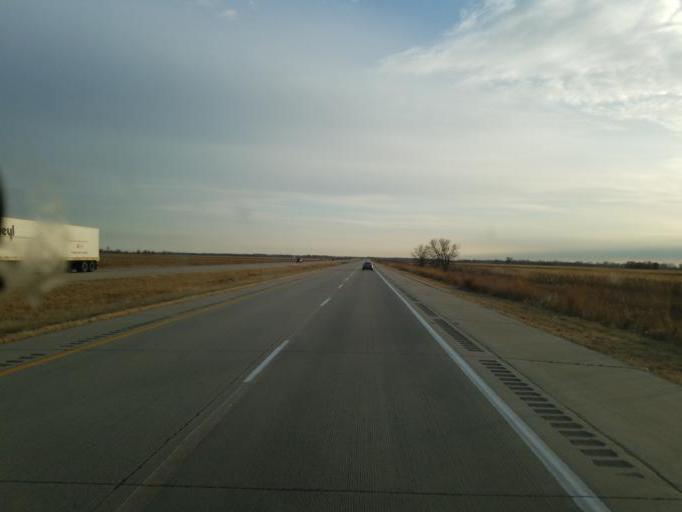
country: US
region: Iowa
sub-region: Monona County
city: Onawa
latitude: 41.8793
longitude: -96.1049
